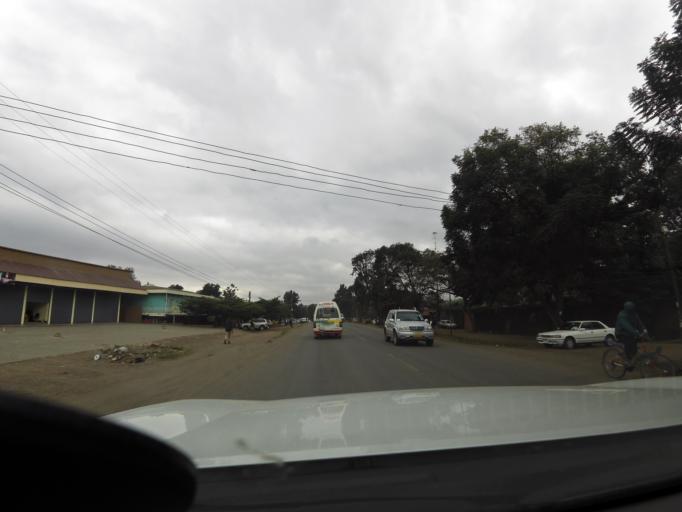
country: TZ
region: Arusha
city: Arusha
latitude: -3.3627
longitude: 36.6699
